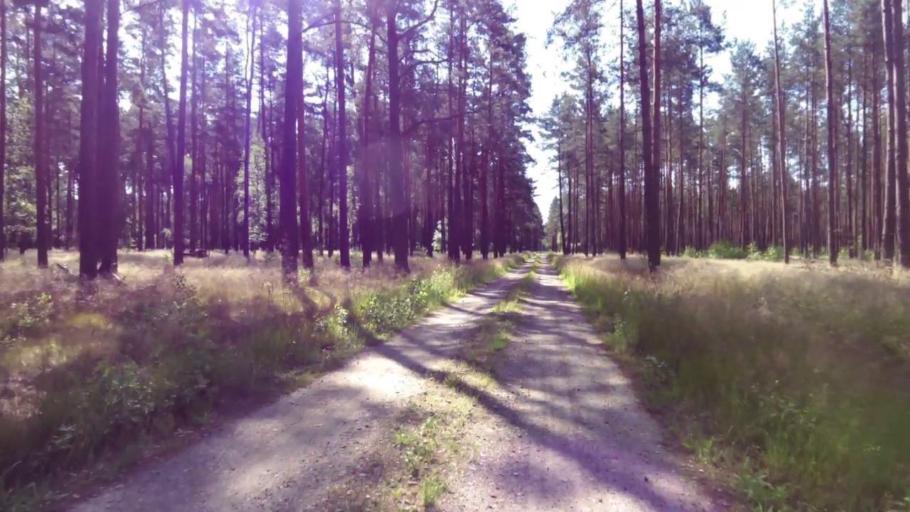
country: PL
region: West Pomeranian Voivodeship
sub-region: Powiat swidwinski
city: Polczyn-Zdroj
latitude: 53.8657
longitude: 16.1235
